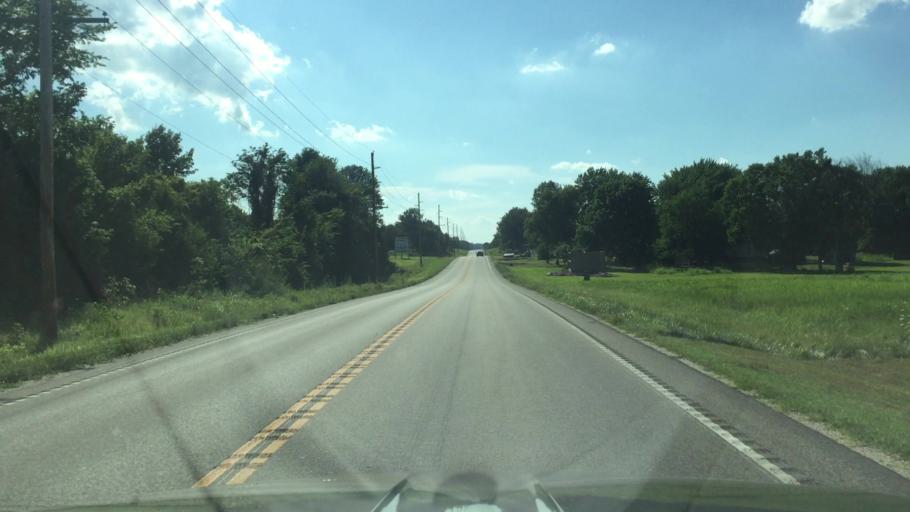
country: US
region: Missouri
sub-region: Morgan County
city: Versailles
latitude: 38.3975
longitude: -92.7288
